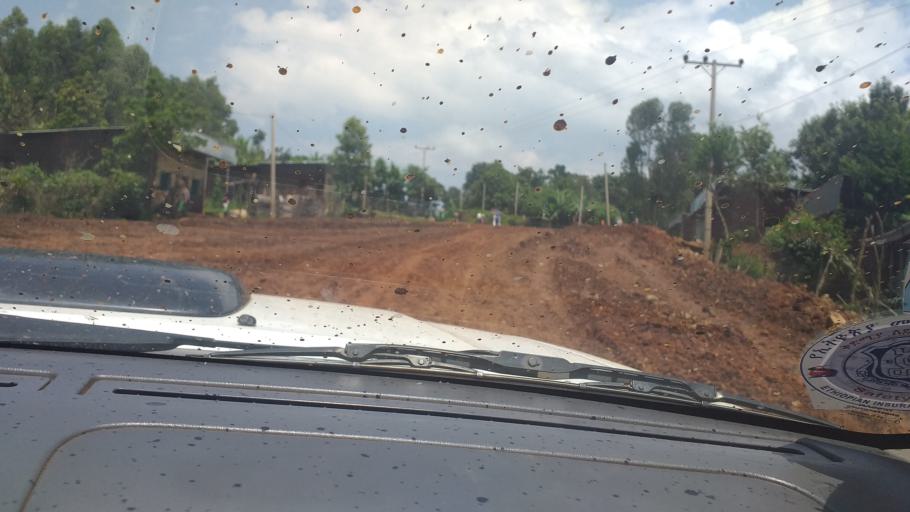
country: ET
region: Southern Nations, Nationalities, and People's Region
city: Bako
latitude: 5.9645
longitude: 36.5265
